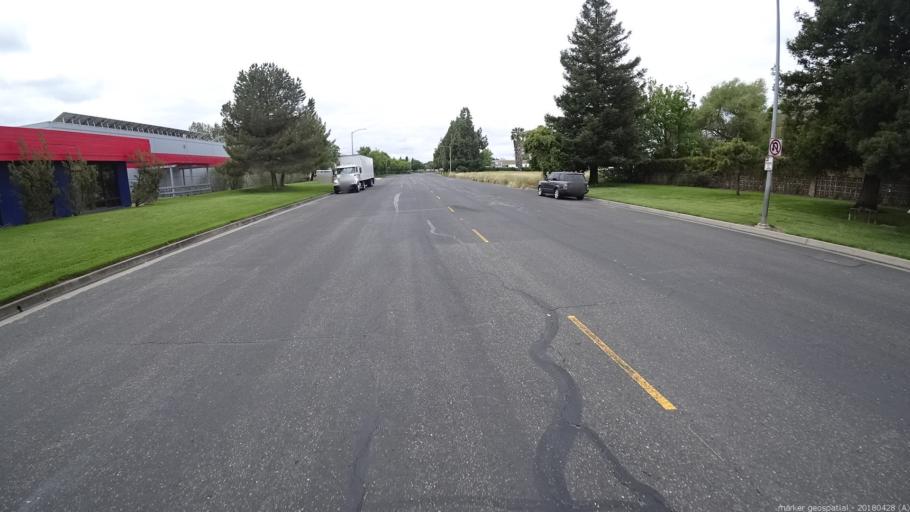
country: US
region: California
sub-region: Yolo County
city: West Sacramento
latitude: 38.5651
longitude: -121.5709
